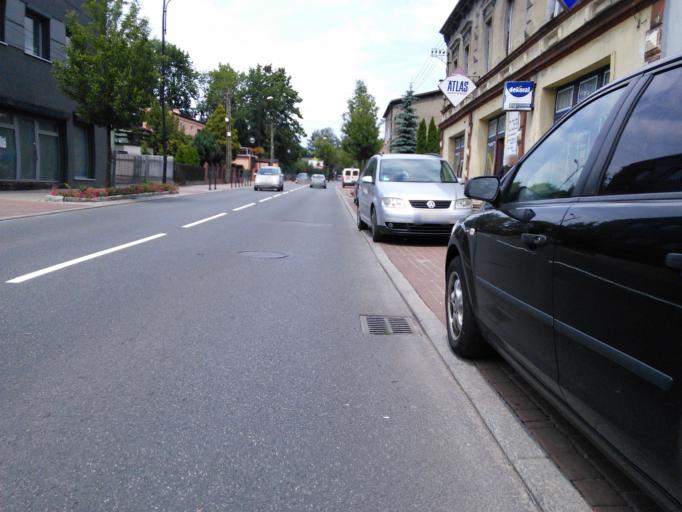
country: PL
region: Silesian Voivodeship
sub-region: Piekary Slaskie
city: Piekary Slaskie
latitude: 50.3885
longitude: 18.9451
